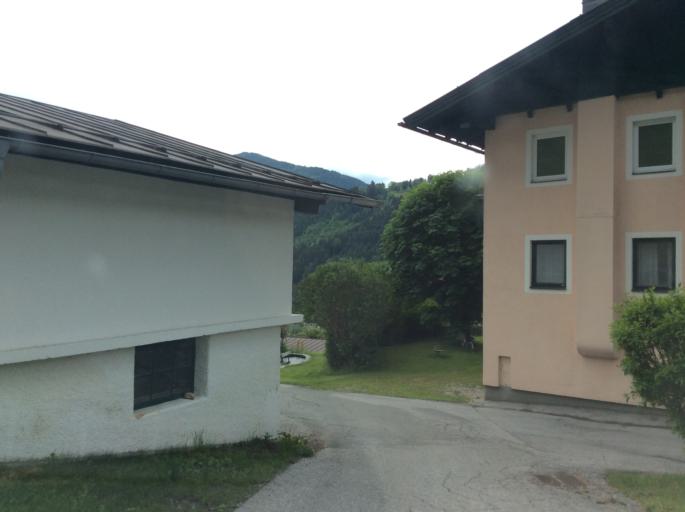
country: AT
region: Styria
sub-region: Politischer Bezirk Liezen
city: Schladming
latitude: 47.3923
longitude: 13.6486
